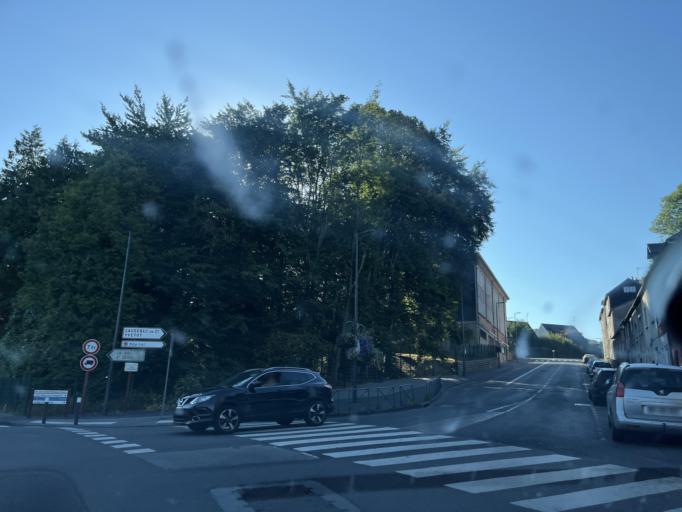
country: FR
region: Haute-Normandie
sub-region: Departement de la Seine-Maritime
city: Lillebonne
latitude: 49.5200
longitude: 0.5388
